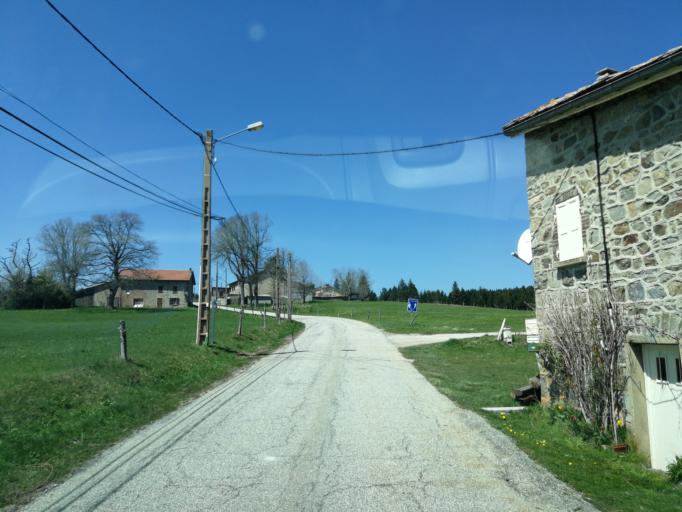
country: FR
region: Auvergne
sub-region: Departement de la Haute-Loire
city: Riotord
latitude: 45.1214
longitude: 4.4088
